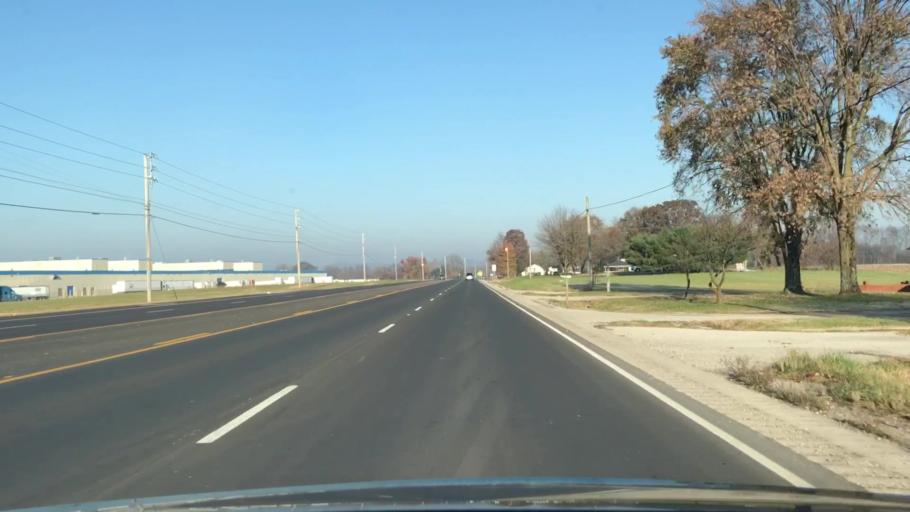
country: US
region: Kentucky
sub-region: Warren County
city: Bowling Green
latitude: 37.0348
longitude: -86.3289
